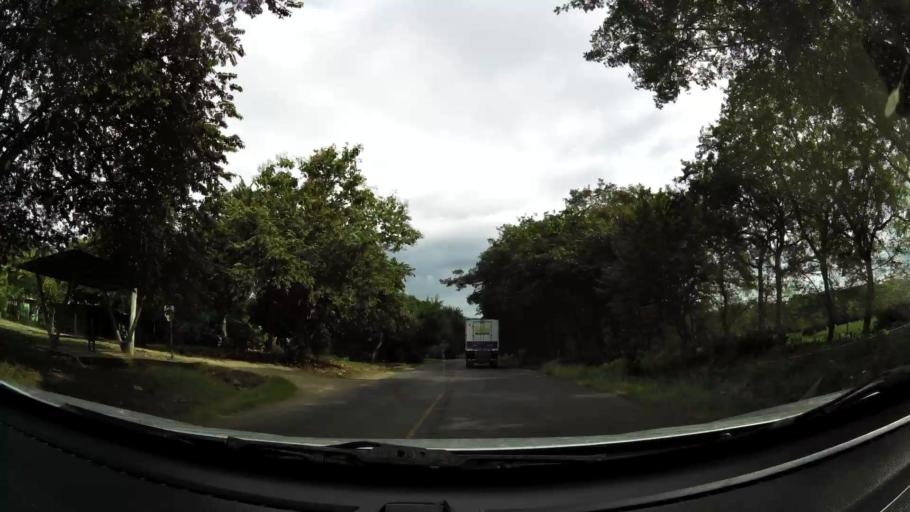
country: CR
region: Guanacaste
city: Juntas
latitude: 10.1728
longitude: -84.9244
